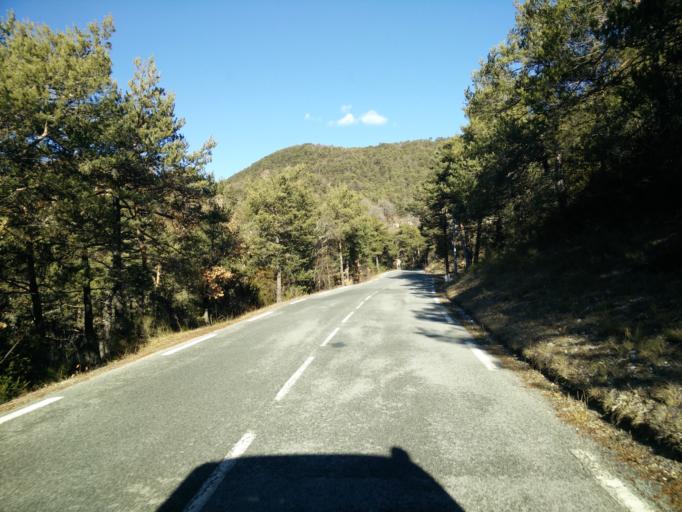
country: FR
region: Provence-Alpes-Cote d'Azur
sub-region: Departement des Alpes-de-Haute-Provence
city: Castellane
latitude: 43.7746
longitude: 6.4477
